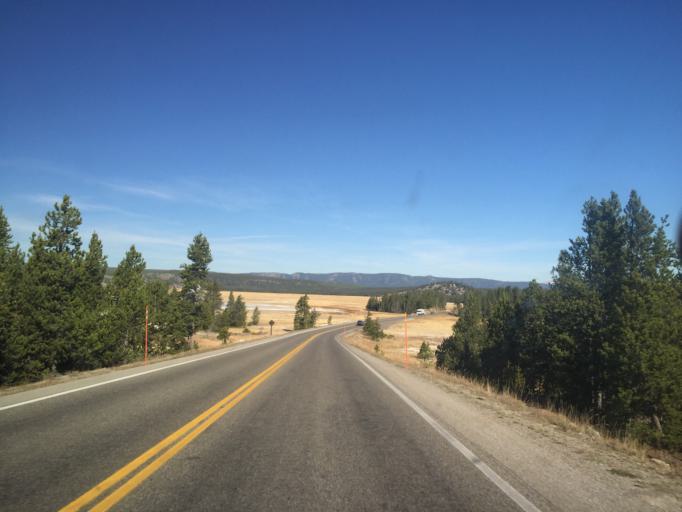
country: US
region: Montana
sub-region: Gallatin County
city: West Yellowstone
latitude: 44.5516
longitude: -110.8058
